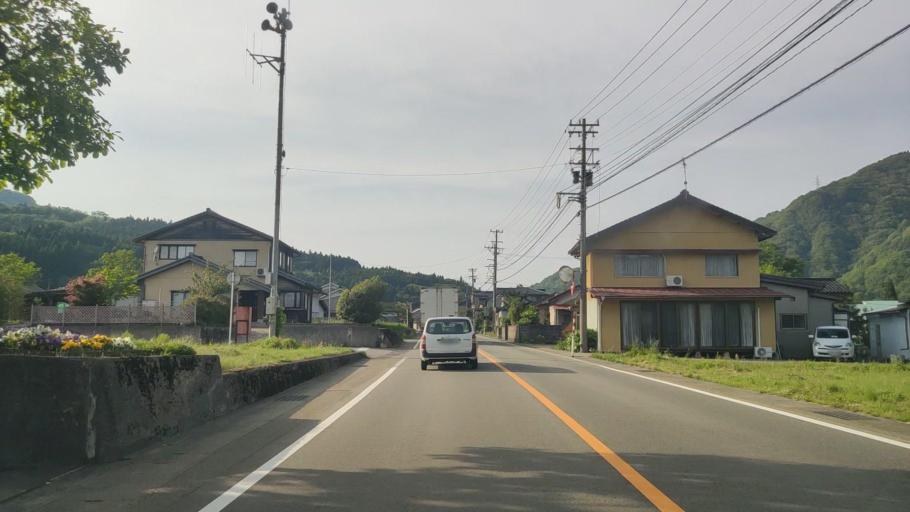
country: JP
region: Toyama
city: Yatsuomachi-higashikumisaka
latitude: 36.5371
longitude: 137.2309
